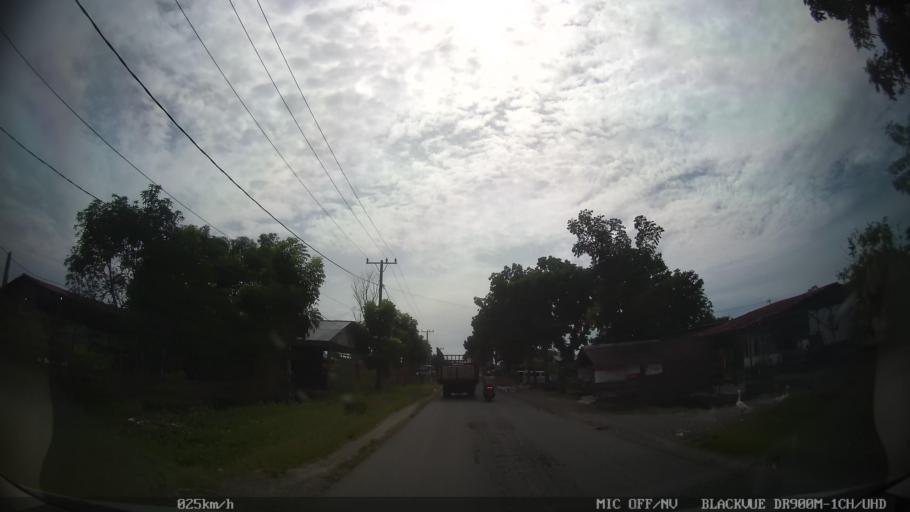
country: ID
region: North Sumatra
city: Percut
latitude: 3.6200
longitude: 98.7790
